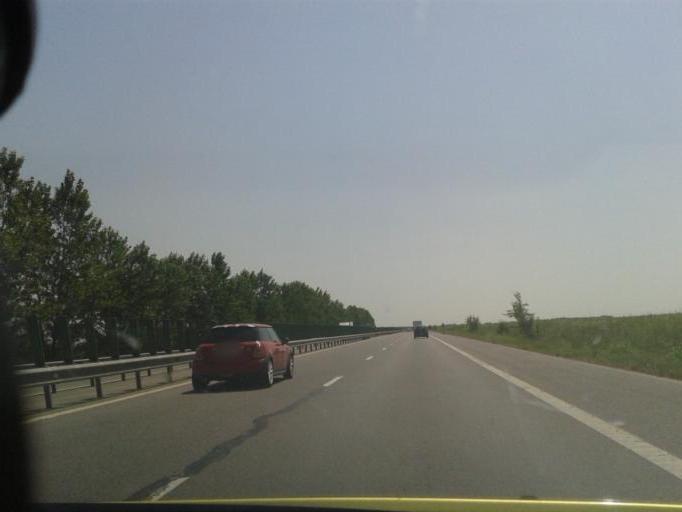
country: RO
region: Calarasi
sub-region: Comuna Tamadau Mare
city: Tamadau Mare
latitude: 44.4456
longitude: 26.5445
